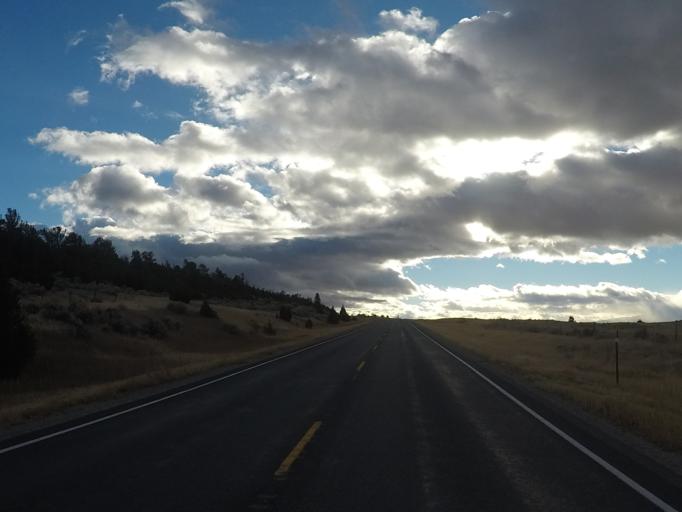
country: US
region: Montana
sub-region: Jefferson County
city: Whitehall
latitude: 45.8963
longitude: -111.9601
